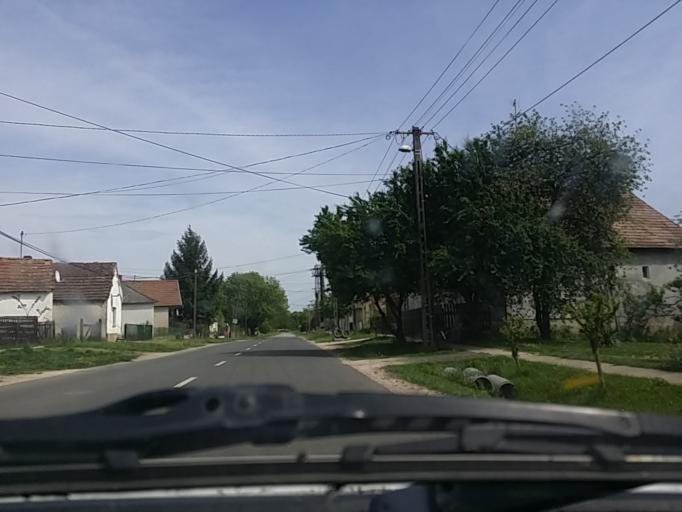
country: HU
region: Baranya
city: Vajszlo
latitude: 45.8551
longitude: 17.9958
